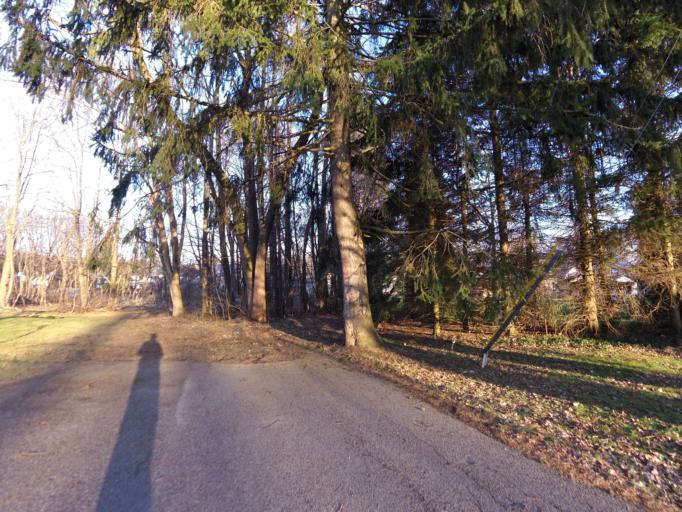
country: US
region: New York
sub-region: Cattaraugus County
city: Franklinville
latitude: 42.3415
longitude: -78.4531
